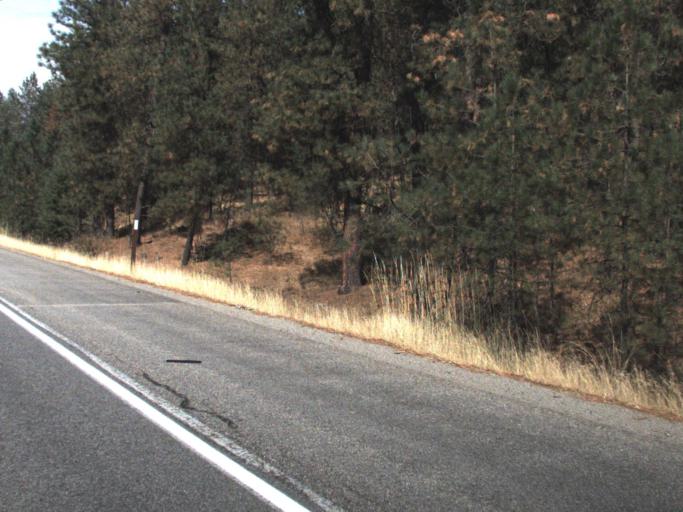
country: US
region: Washington
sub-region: Spokane County
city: Deer Park
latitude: 47.9252
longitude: -117.3505
